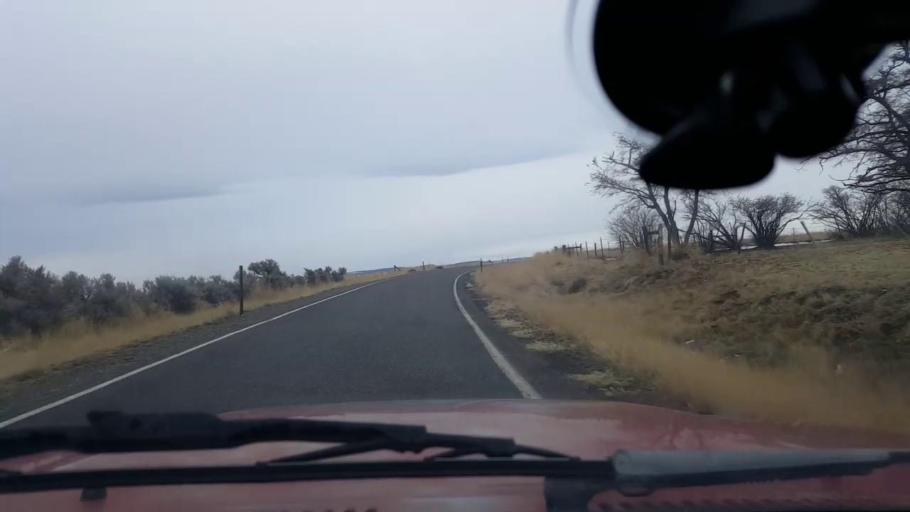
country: US
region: Washington
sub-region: Asotin County
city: Clarkston Heights-Vineland
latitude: 46.3157
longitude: -117.3298
